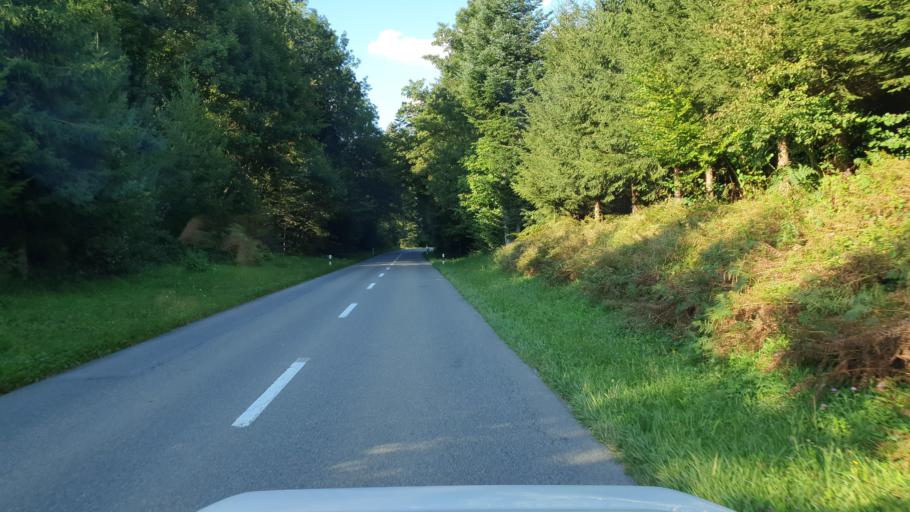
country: CH
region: Aargau
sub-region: Bezirk Bremgarten
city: Bremgarten
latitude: 47.3319
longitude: 8.3304
